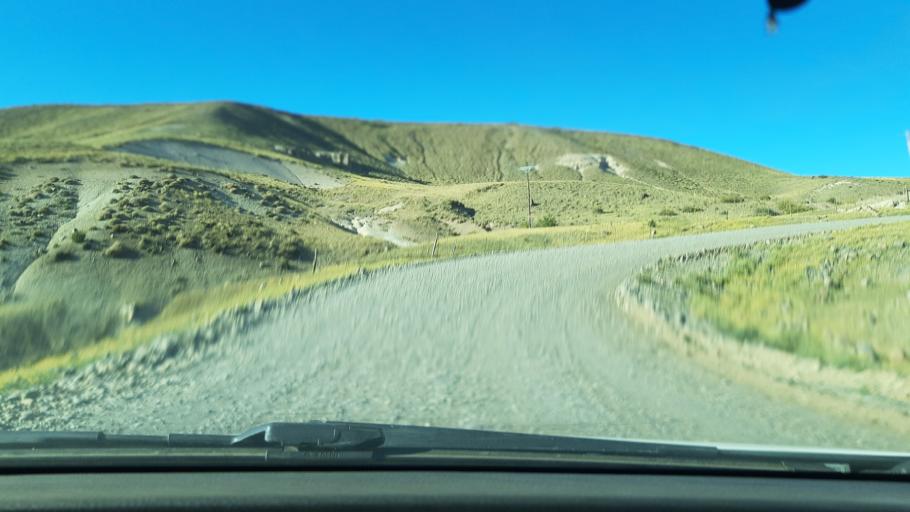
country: AR
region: Neuquen
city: Las Ovejas
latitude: -36.8225
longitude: -70.7070
